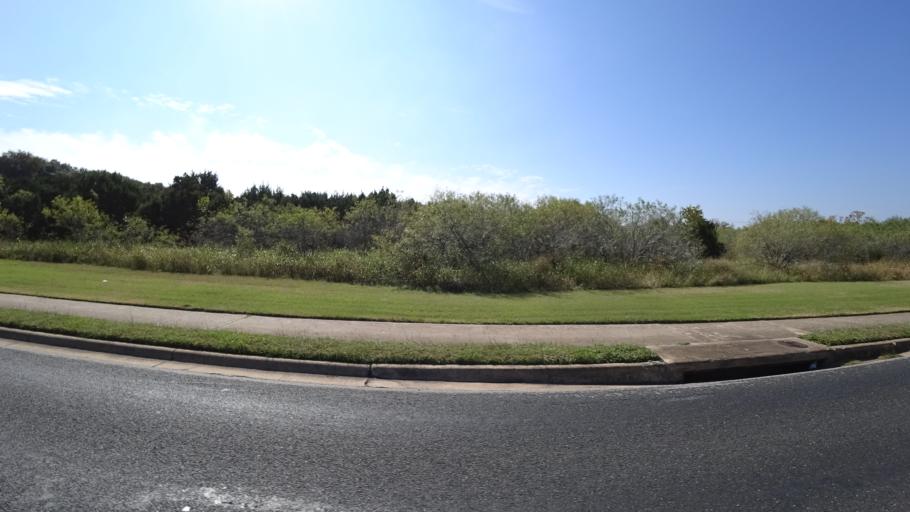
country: US
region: Texas
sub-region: Travis County
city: Shady Hollow
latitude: 30.2097
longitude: -97.8214
